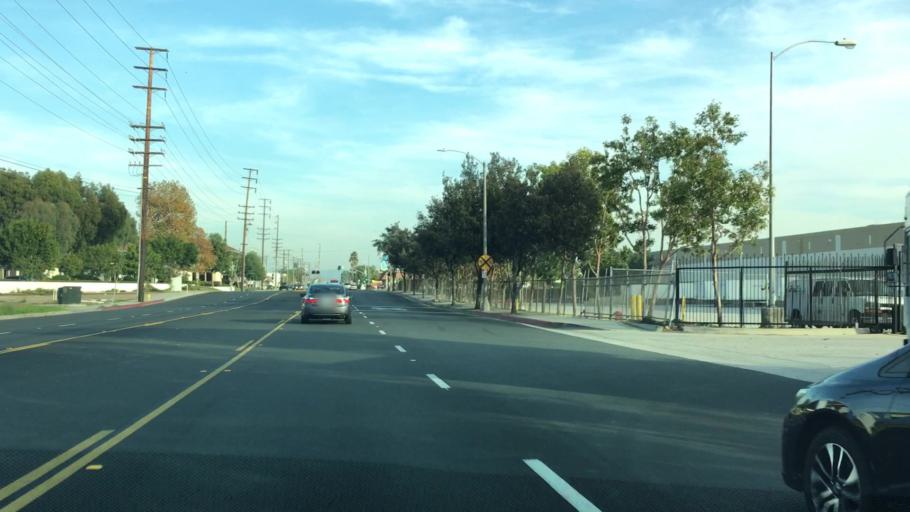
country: US
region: California
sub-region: Orange County
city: La Habra
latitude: 33.9246
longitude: -117.9271
